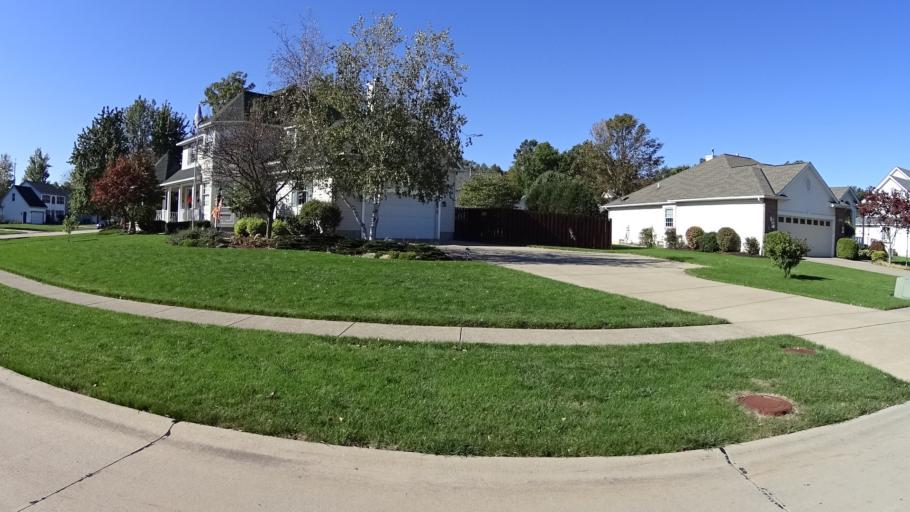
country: US
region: Ohio
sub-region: Lorain County
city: Amherst
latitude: 41.4083
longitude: -82.2461
